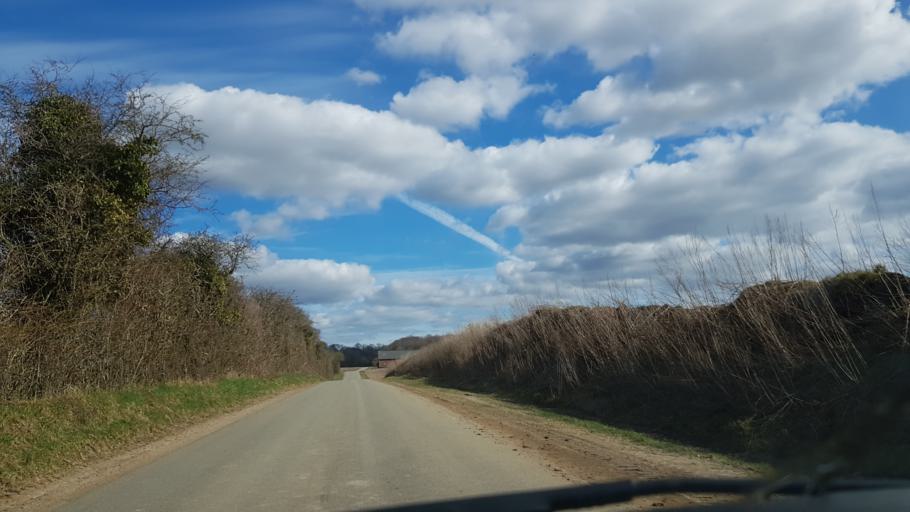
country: DK
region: South Denmark
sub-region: Kolding Kommune
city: Vamdrup
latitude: 55.3563
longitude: 9.3692
